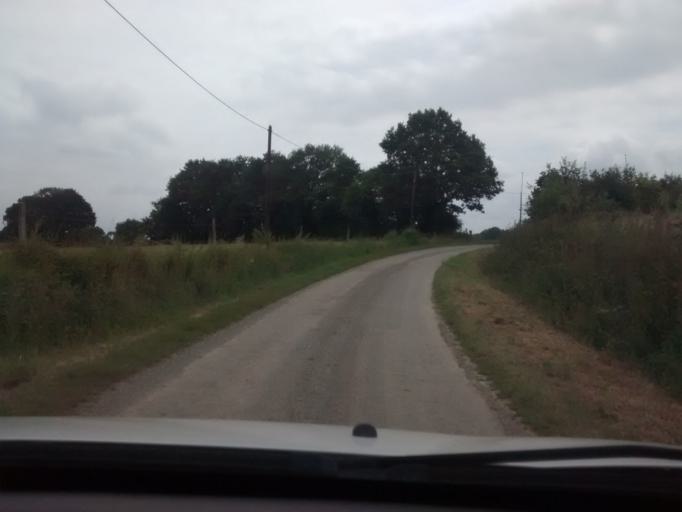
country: FR
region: Brittany
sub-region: Departement d'Ille-et-Vilaine
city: Servon-sur-Vilaine
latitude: 48.1368
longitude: -1.4818
